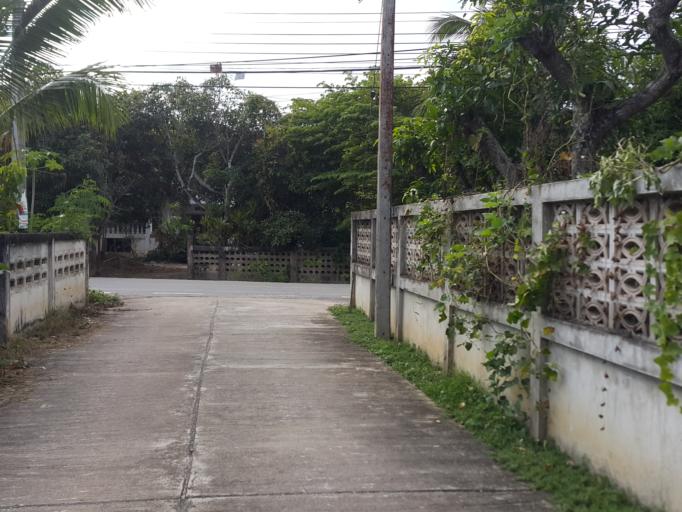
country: TH
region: Chiang Mai
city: San Sai
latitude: 18.8833
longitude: 99.1029
